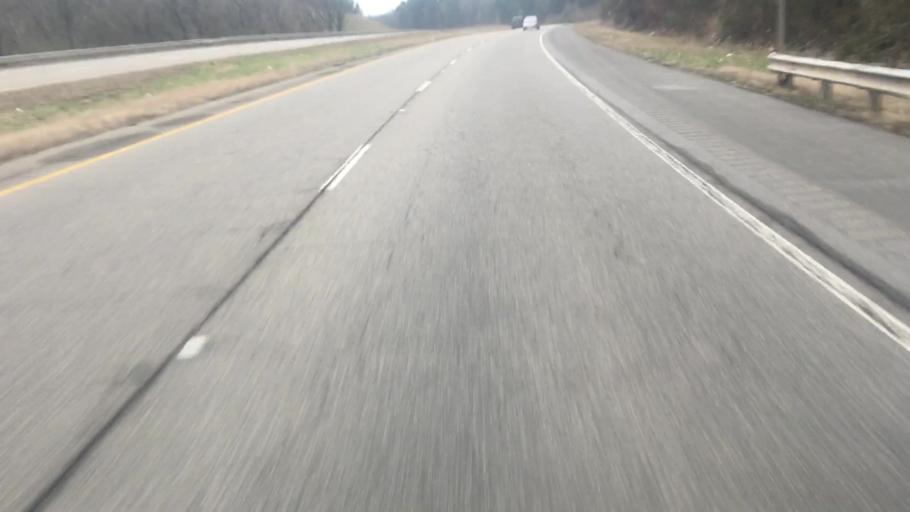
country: US
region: Alabama
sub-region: Walker County
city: Cordova
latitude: 33.8129
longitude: -87.1479
